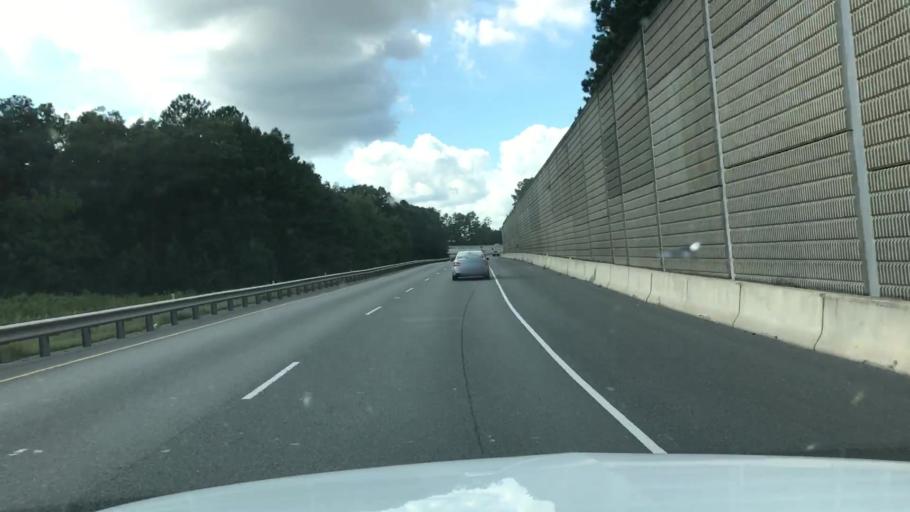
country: US
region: Virginia
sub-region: Henrico County
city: Short Pump
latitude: 37.6578
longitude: -77.6046
